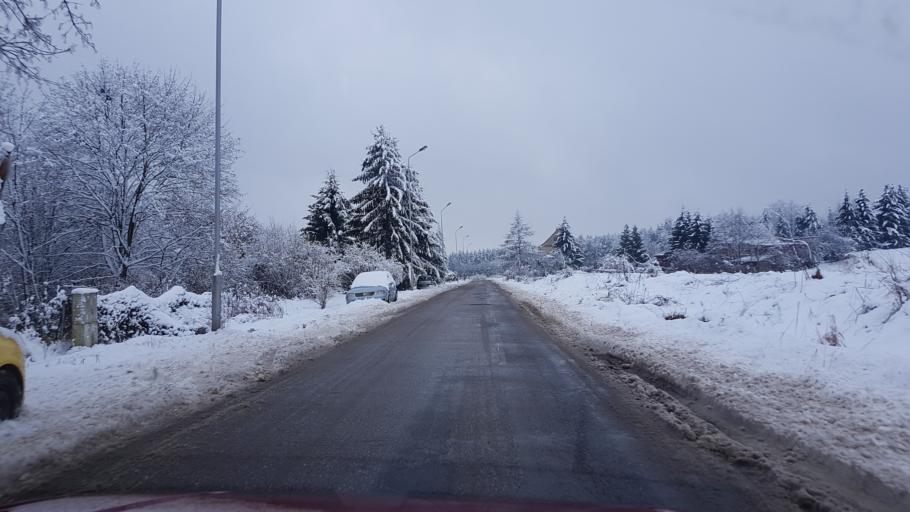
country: PL
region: West Pomeranian Voivodeship
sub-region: Powiat drawski
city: Zlocieniec
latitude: 53.5235
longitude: 16.0072
